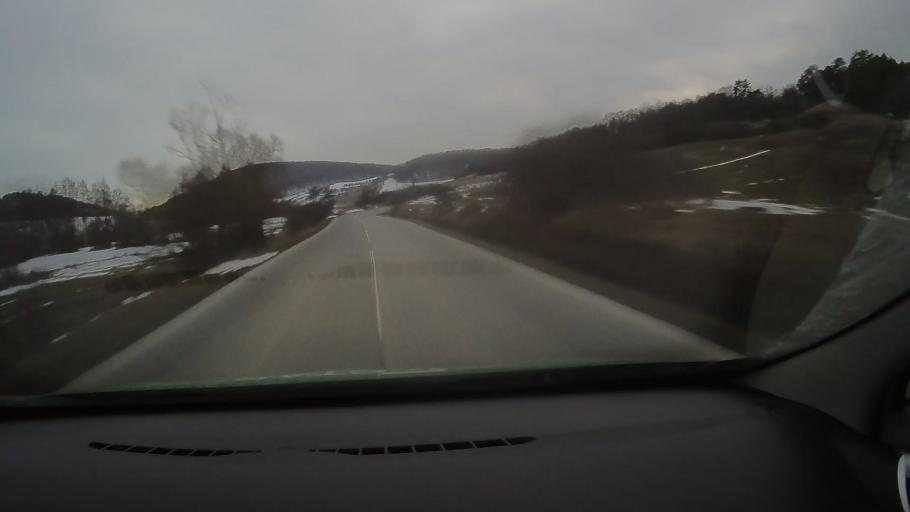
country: RO
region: Harghita
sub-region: Comuna Mugeni
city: Mugeni
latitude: 46.2333
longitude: 25.2441
